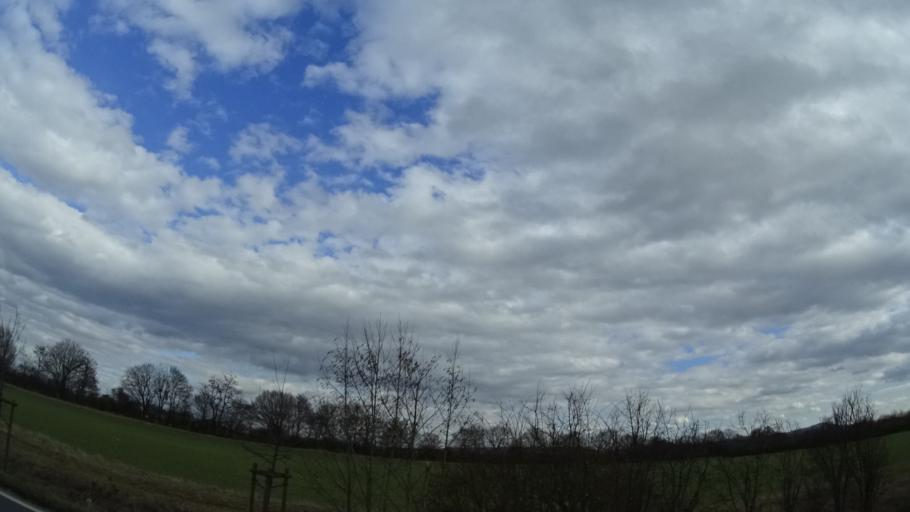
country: DE
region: Hesse
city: Biebesheim
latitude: 49.7919
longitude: 8.4848
